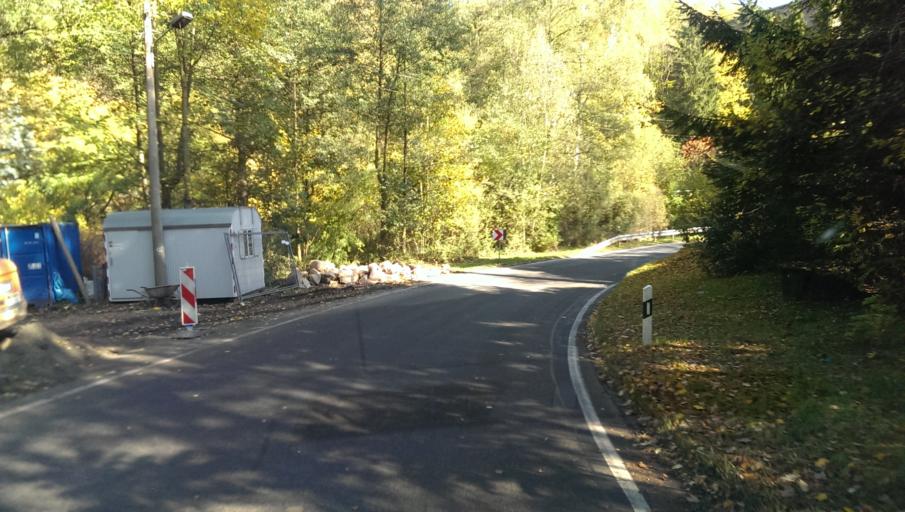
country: DE
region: Saxony
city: Waldheim
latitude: 51.0661
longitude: 13.0116
